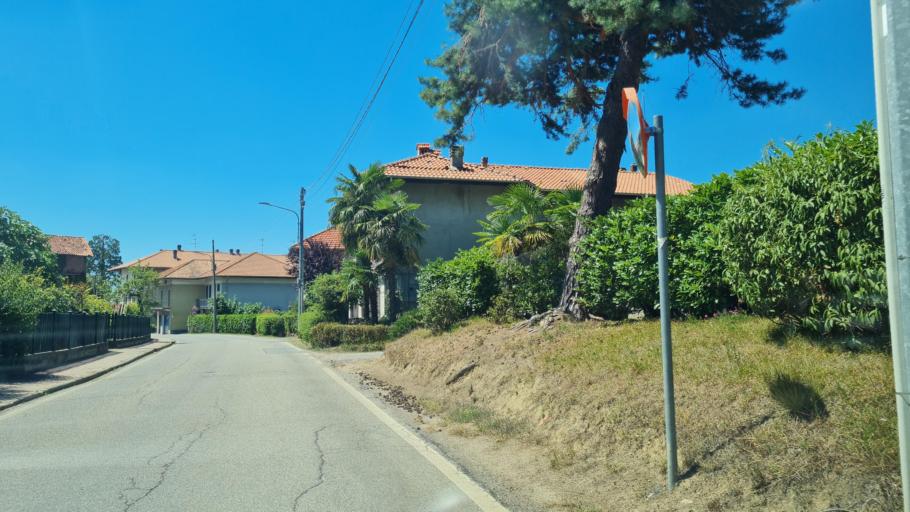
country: IT
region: Piedmont
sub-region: Provincia di Biella
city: Lessona
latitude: 45.5929
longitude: 8.1921
